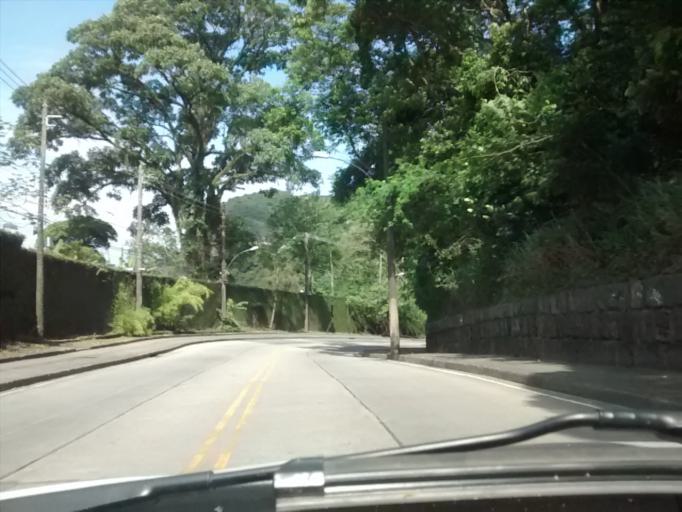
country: BR
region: Rio de Janeiro
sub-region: Rio De Janeiro
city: Rio de Janeiro
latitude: -22.9606
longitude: -43.2718
